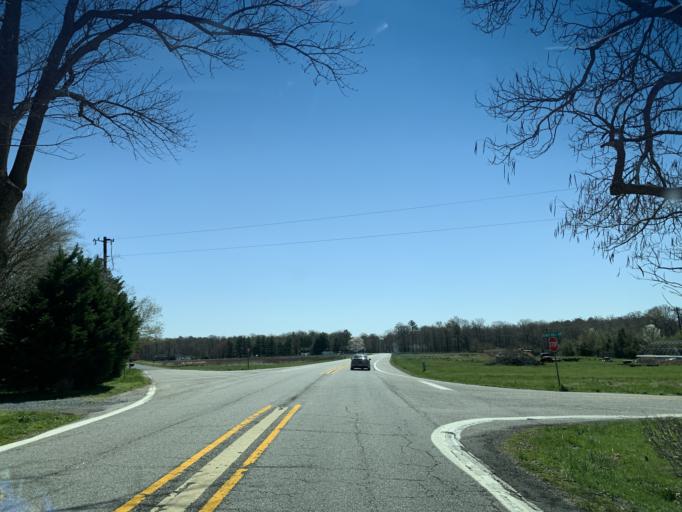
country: US
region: Maryland
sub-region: Queen Anne's County
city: Centreville
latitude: 38.9785
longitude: -76.0107
